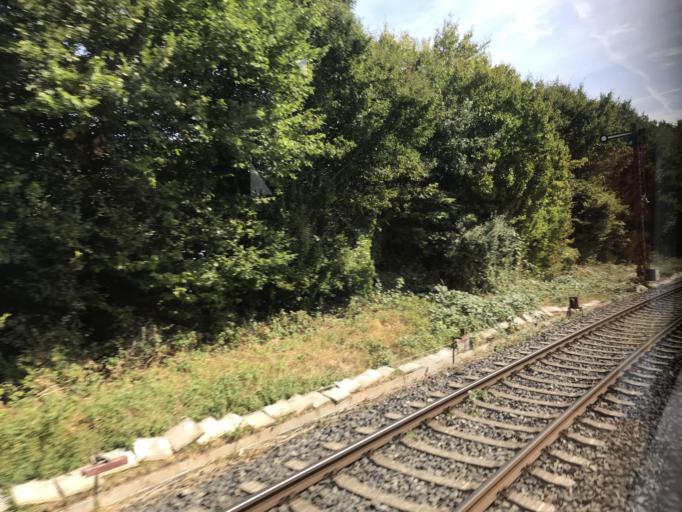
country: DE
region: Hesse
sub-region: Regierungsbezirk Giessen
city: Limburg an der Lahn
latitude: 50.3937
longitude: 8.0501
